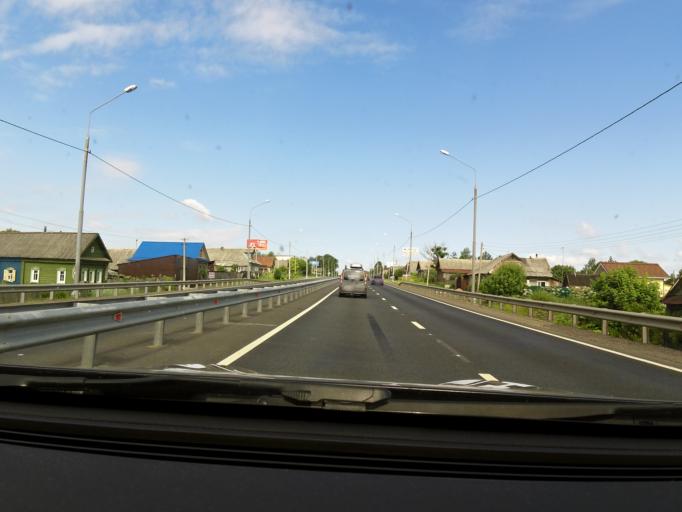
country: RU
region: Tverskaya
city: Emmaus
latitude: 56.7749
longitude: 36.1254
